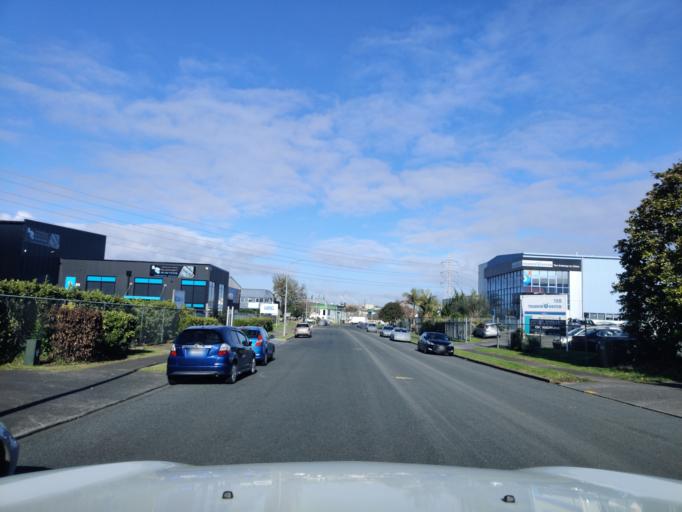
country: NZ
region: Auckland
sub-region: Auckland
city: Manukau City
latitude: -36.9399
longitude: 174.8818
